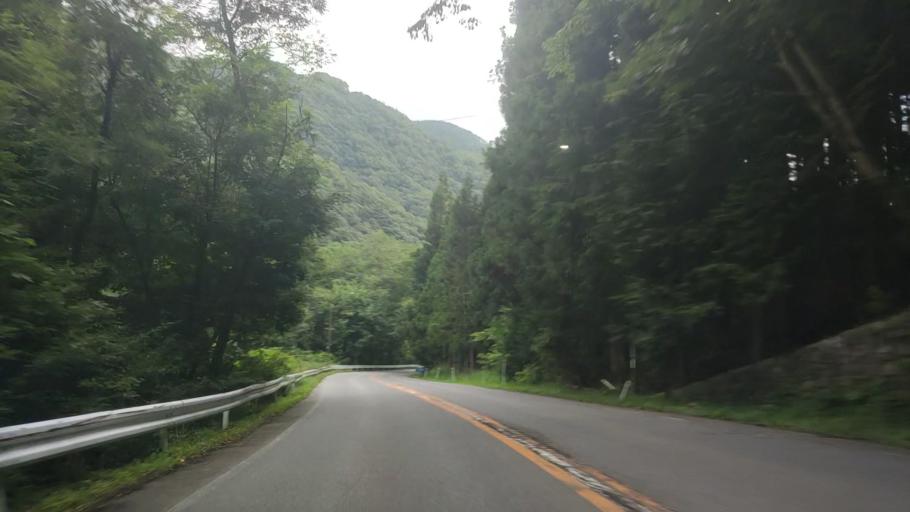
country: JP
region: Gunma
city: Omamacho-omama
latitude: 36.6075
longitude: 139.4037
